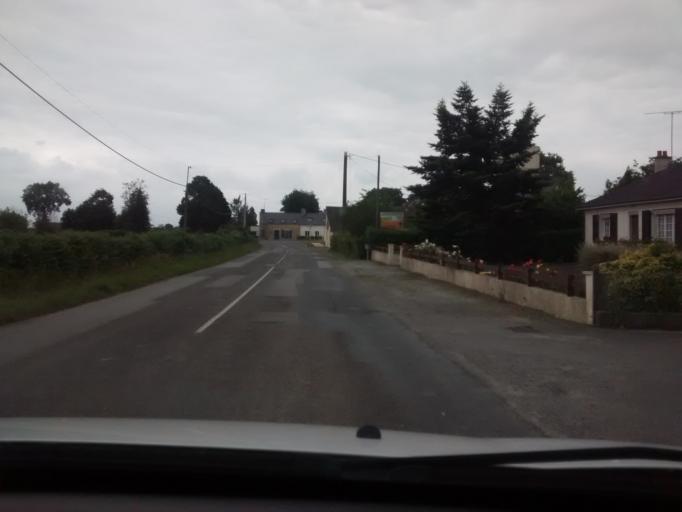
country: FR
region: Brittany
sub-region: Departement d'Ille-et-Vilaine
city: La Bouexiere
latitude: 48.1742
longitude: -1.4358
